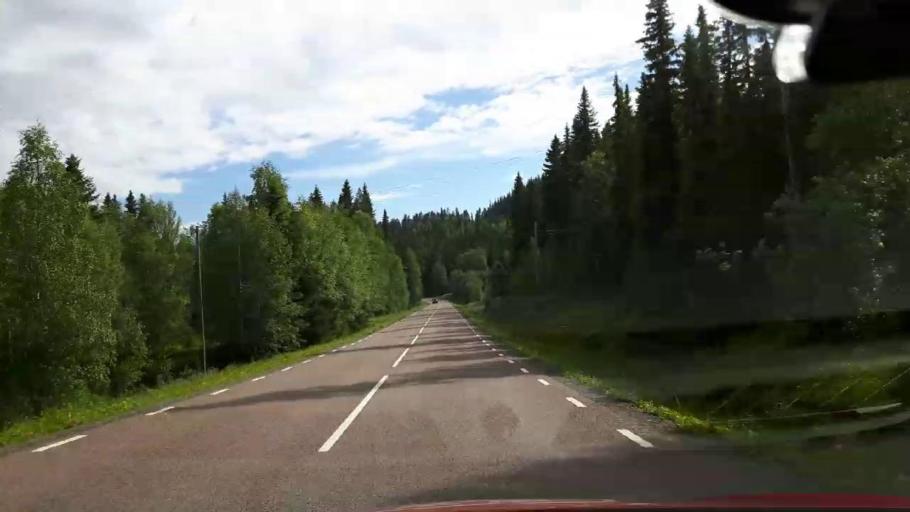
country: SE
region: Jaemtland
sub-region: Krokoms Kommun
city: Valla
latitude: 63.9210
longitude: 14.2144
